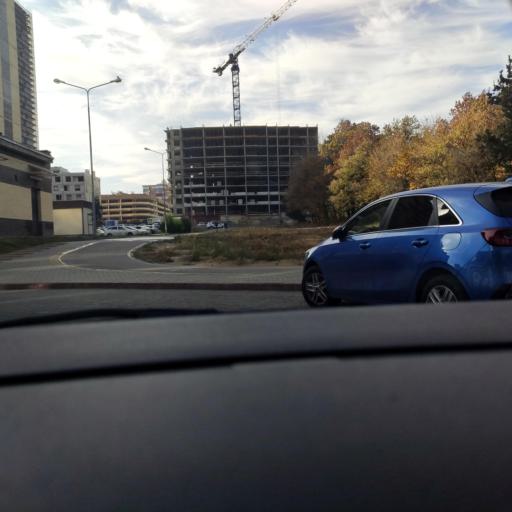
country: RU
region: Voronezj
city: Voronezh
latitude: 51.7164
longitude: 39.1940
